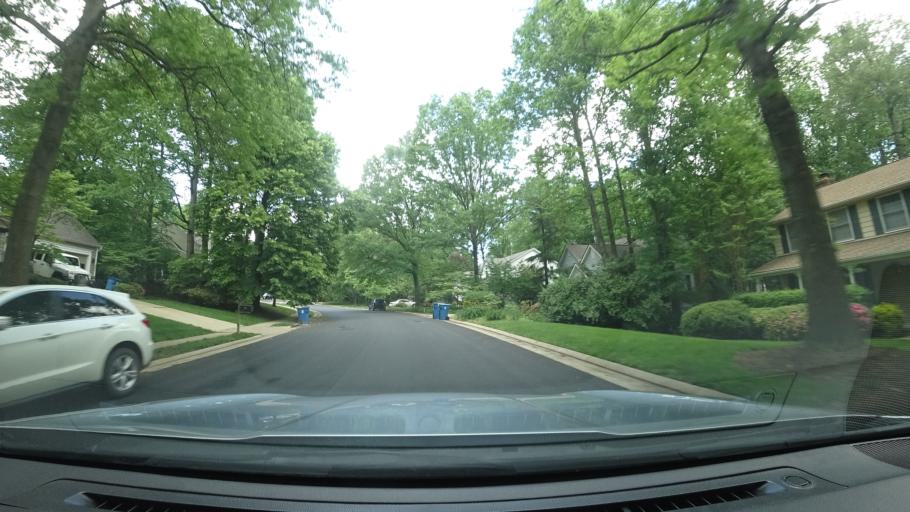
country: US
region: Virginia
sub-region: Fairfax County
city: Reston
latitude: 38.9728
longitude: -77.3493
